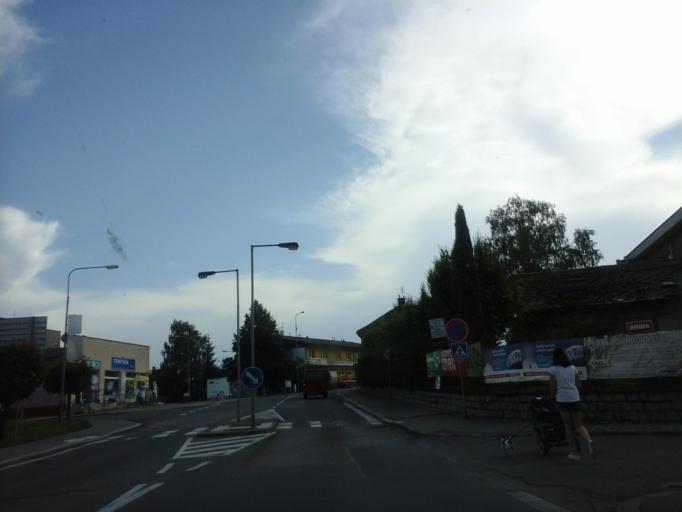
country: CZ
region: Pardubicky
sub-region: Okres Usti nad Orlici
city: Lanskroun
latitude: 49.9098
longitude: 16.6077
